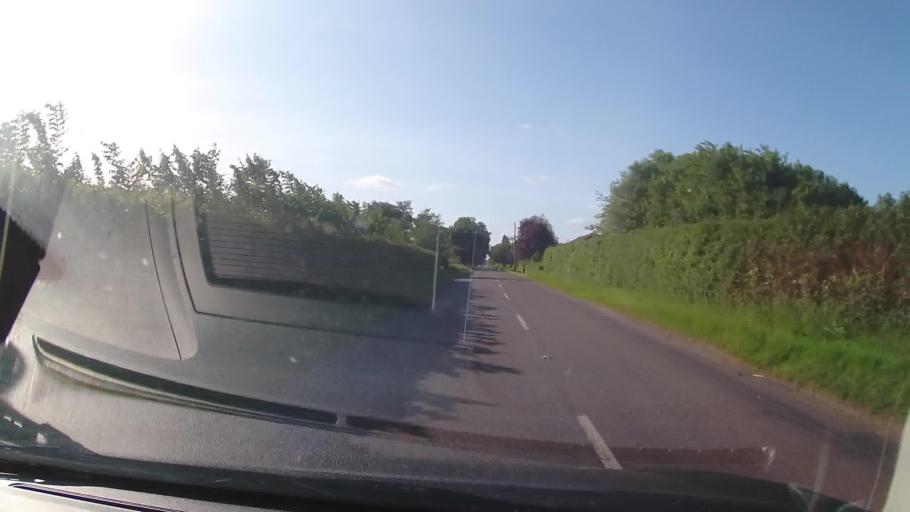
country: GB
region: England
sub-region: Shropshire
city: Shawbury
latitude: 52.7832
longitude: -2.6451
